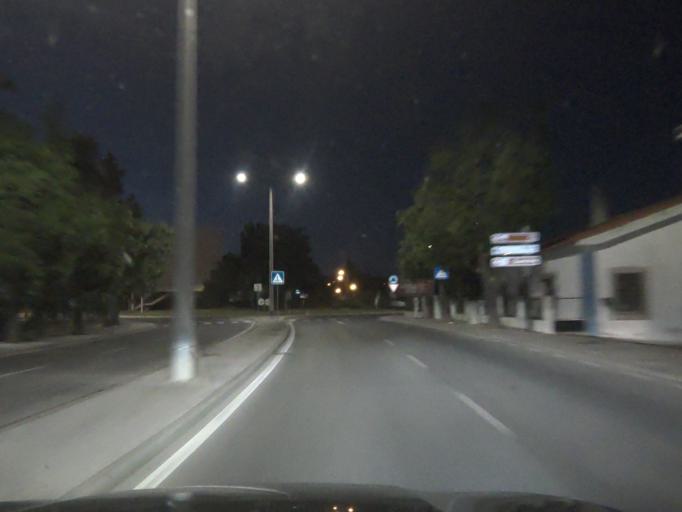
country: PT
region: Faro
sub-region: Loule
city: Loule
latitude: 37.1455
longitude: -8.0119
